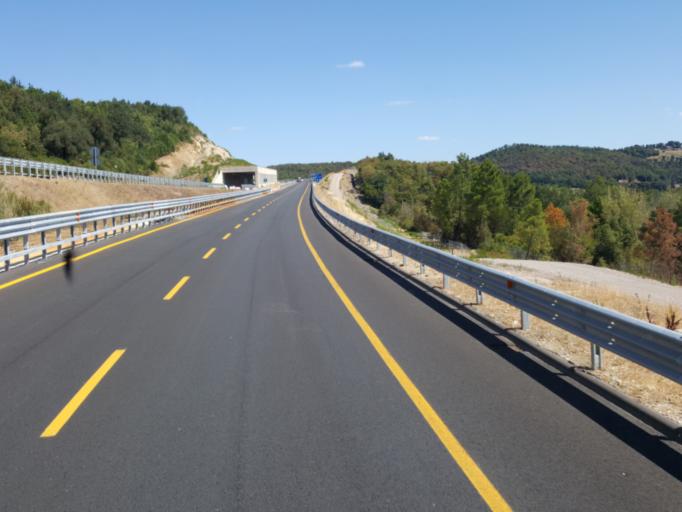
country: IT
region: Tuscany
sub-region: Provincia di Grosseto
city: Civitella Marittima
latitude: 43.0882
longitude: 11.2953
